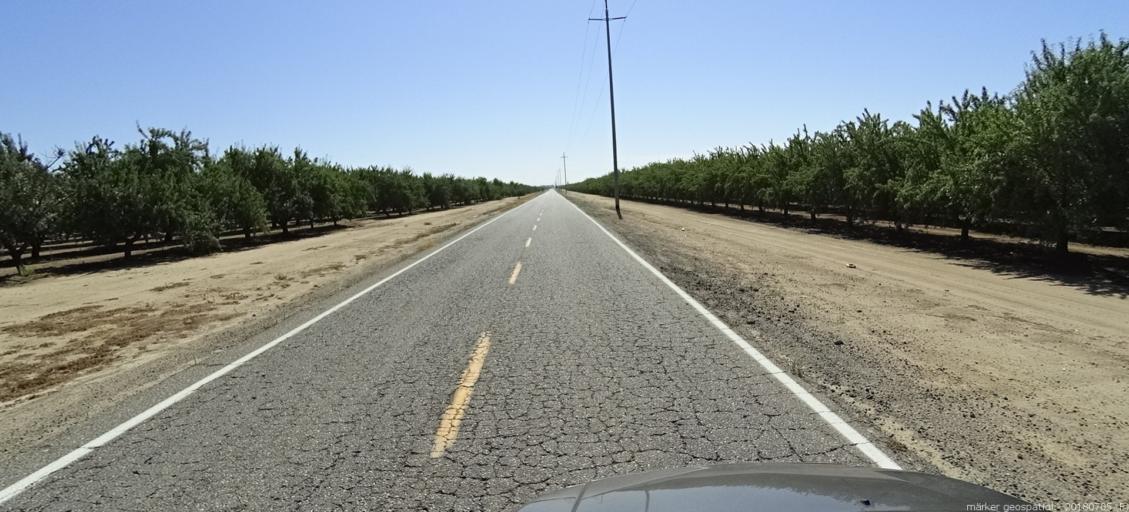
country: US
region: California
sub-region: Madera County
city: Fairmead
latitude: 37.1272
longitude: -120.1830
